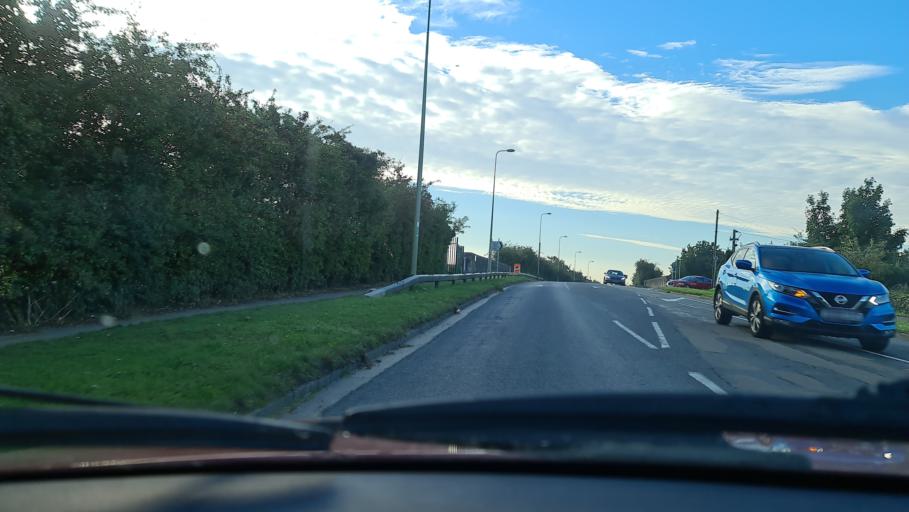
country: GB
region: England
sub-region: Oxfordshire
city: Kidlington
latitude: 51.8318
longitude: -1.3009
